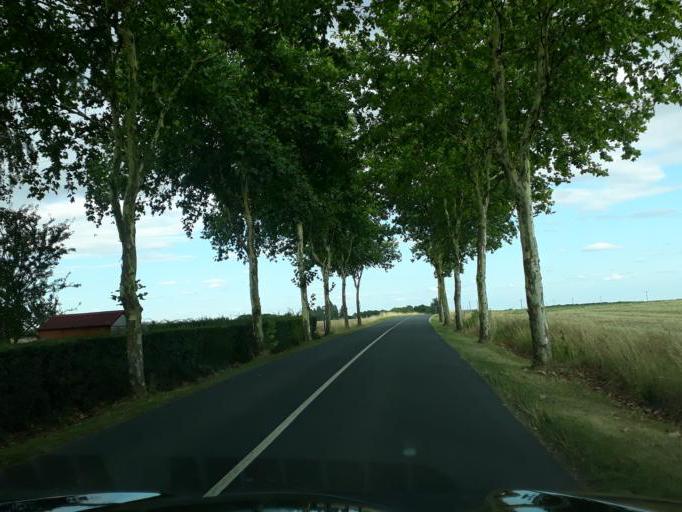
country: FR
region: Centre
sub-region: Departement du Loir-et-Cher
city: Oucques
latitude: 47.8203
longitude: 1.3964
